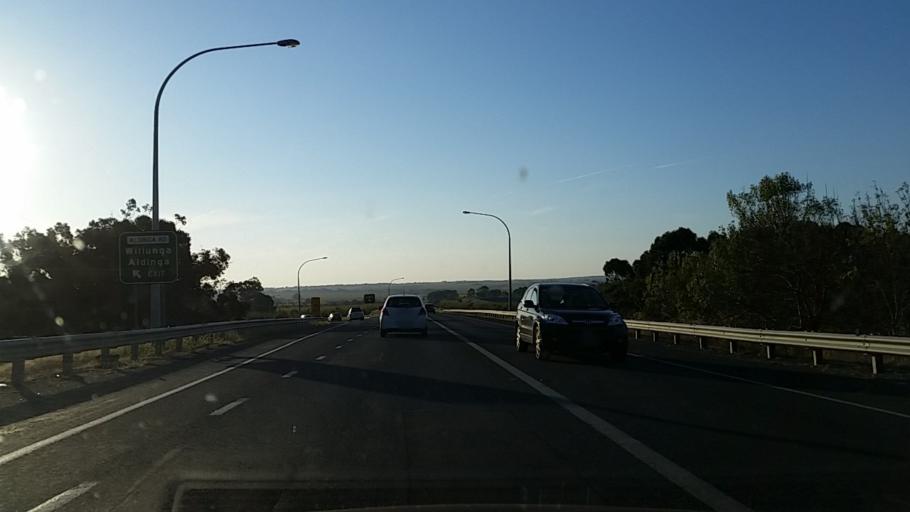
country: AU
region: South Australia
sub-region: Onkaparinga
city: McLaren Vale
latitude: -35.2722
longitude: 138.5391
